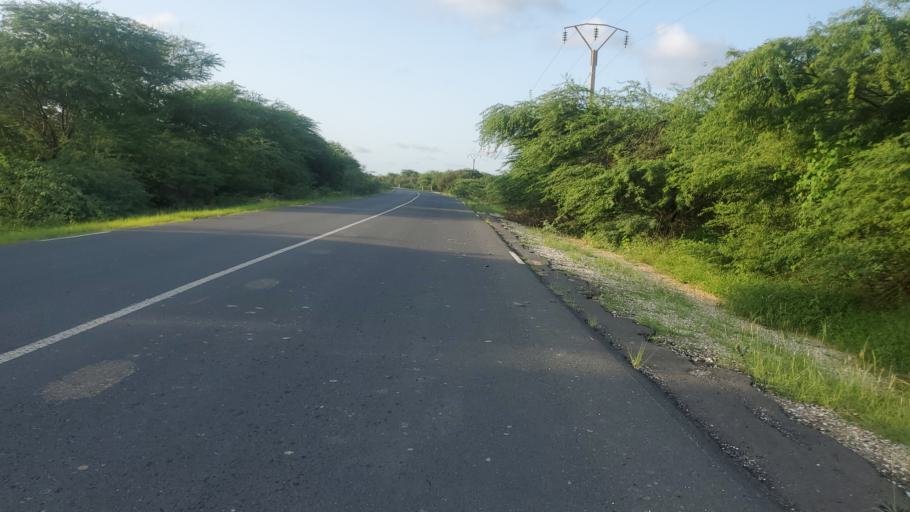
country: SN
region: Saint-Louis
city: Saint-Louis
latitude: 16.1931
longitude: -16.4091
